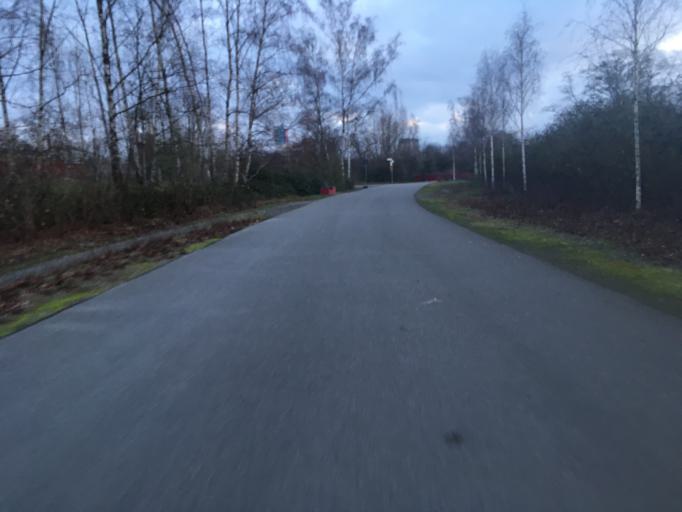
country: DE
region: North Rhine-Westphalia
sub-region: Regierungsbezirk Dusseldorf
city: Essen
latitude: 51.4644
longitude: 6.9967
